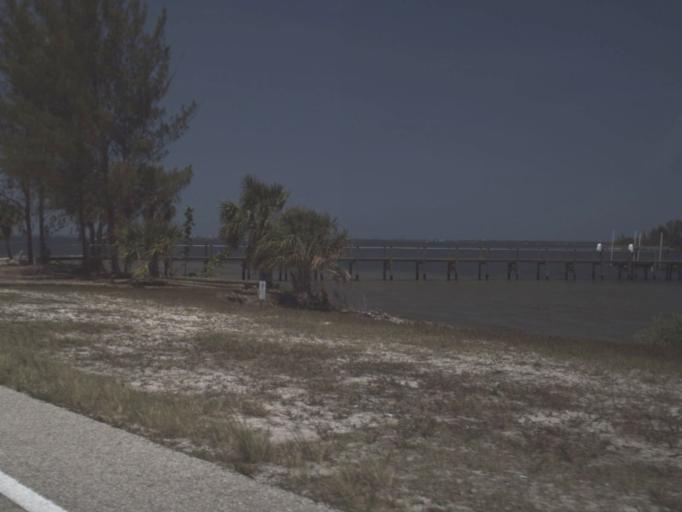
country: US
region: Florida
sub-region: Brevard County
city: Grant-Valkaria
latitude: 27.9628
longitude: -80.5410
